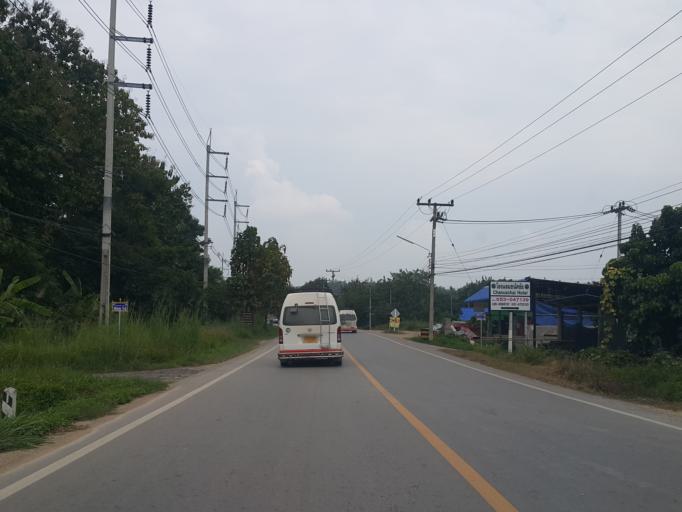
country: TH
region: Chiang Mai
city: Mae Taeng
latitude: 19.0880
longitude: 98.8917
